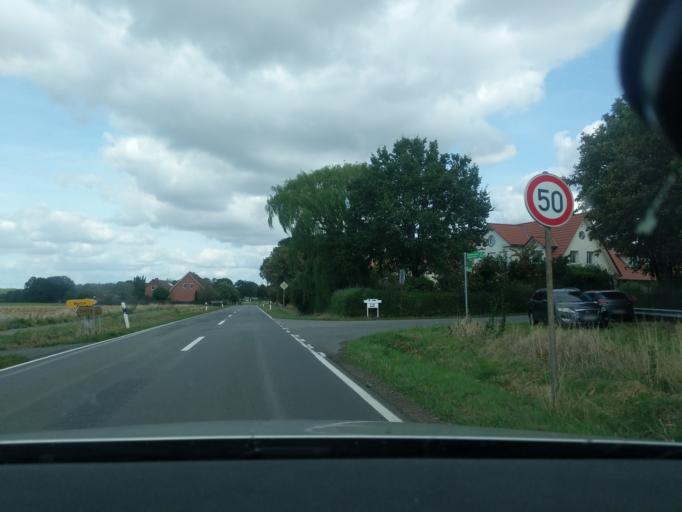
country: DE
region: Lower Saxony
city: Wietzen
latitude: 52.7414
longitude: 9.0654
